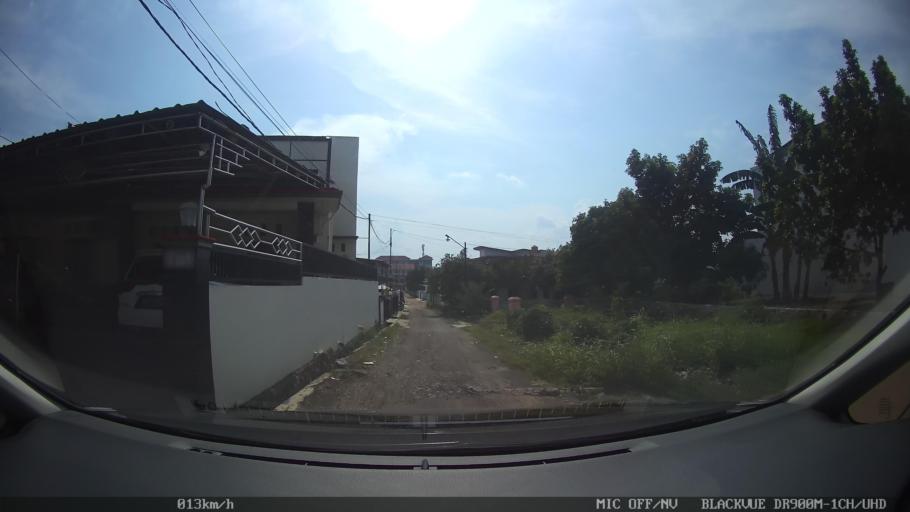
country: ID
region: Lampung
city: Kedaton
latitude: -5.3848
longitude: 105.2374
